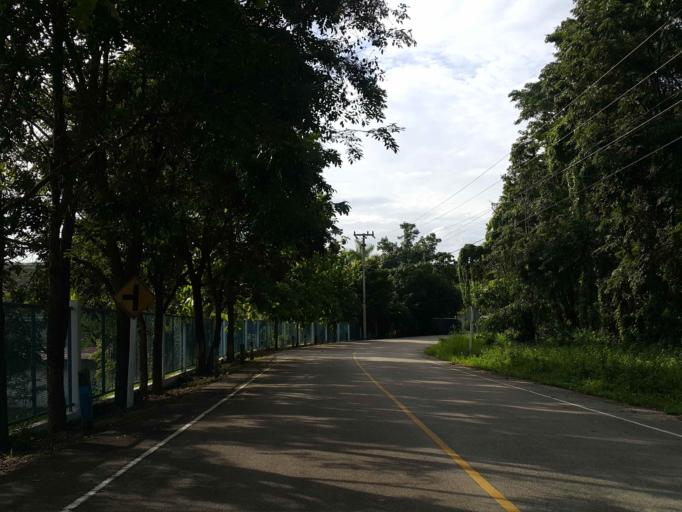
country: TH
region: Chiang Mai
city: San Sai
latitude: 18.9365
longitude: 99.1409
